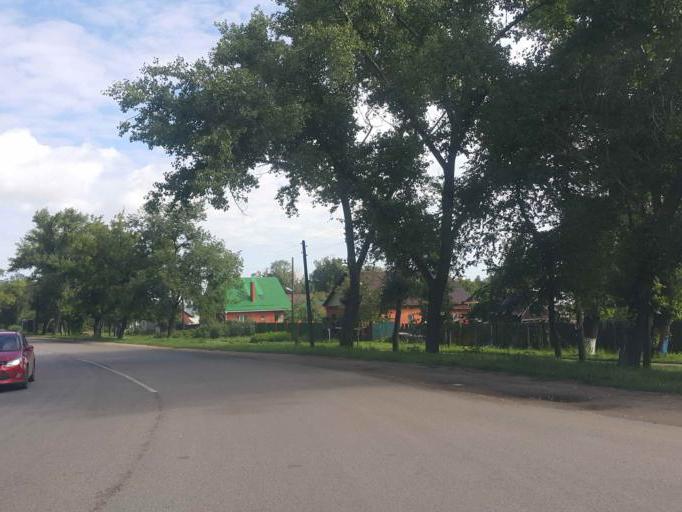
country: RU
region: Tambov
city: Pokrovo-Prigorodnoye
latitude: 52.7103
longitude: 41.4207
